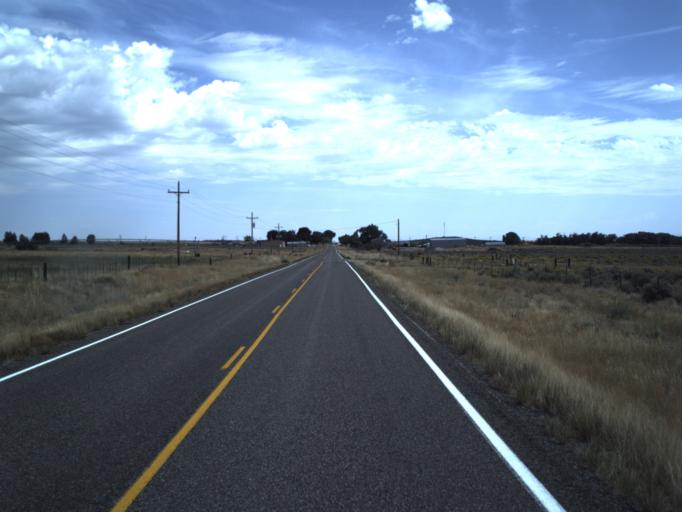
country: US
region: Idaho
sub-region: Cassia County
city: Burley
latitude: 41.8168
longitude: -113.3413
